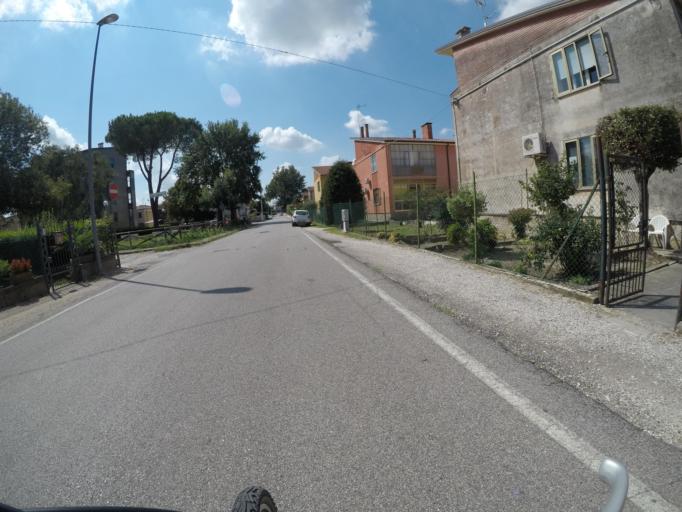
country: IT
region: Veneto
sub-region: Provincia di Rovigo
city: Lendinara
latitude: 45.0879
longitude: 11.5897
